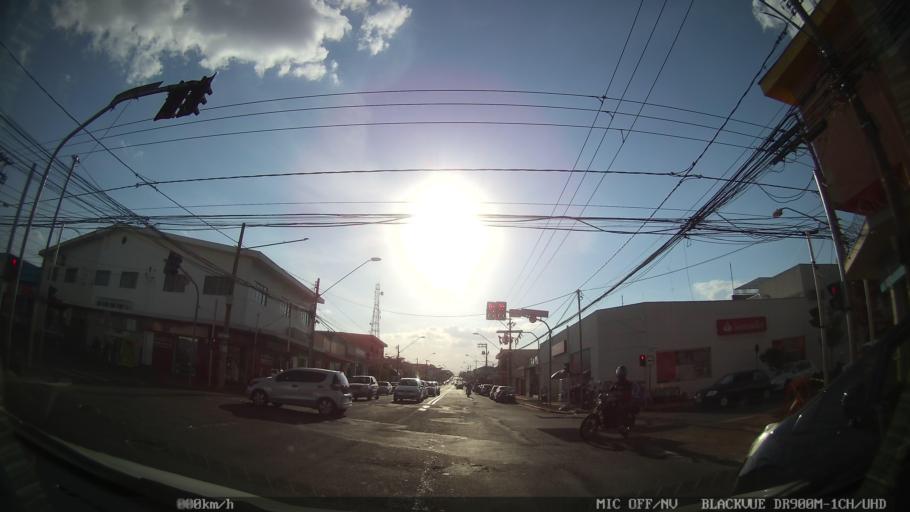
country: BR
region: Sao Paulo
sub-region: Ribeirao Preto
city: Ribeirao Preto
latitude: -21.1556
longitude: -47.8198
